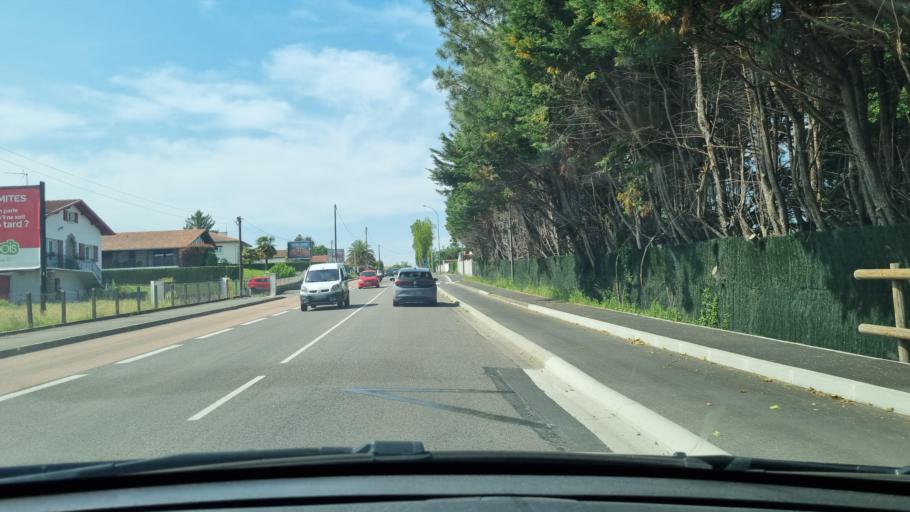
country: FR
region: Aquitaine
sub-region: Departement des Pyrenees-Atlantiques
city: Anglet
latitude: 43.4697
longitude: -1.4978
